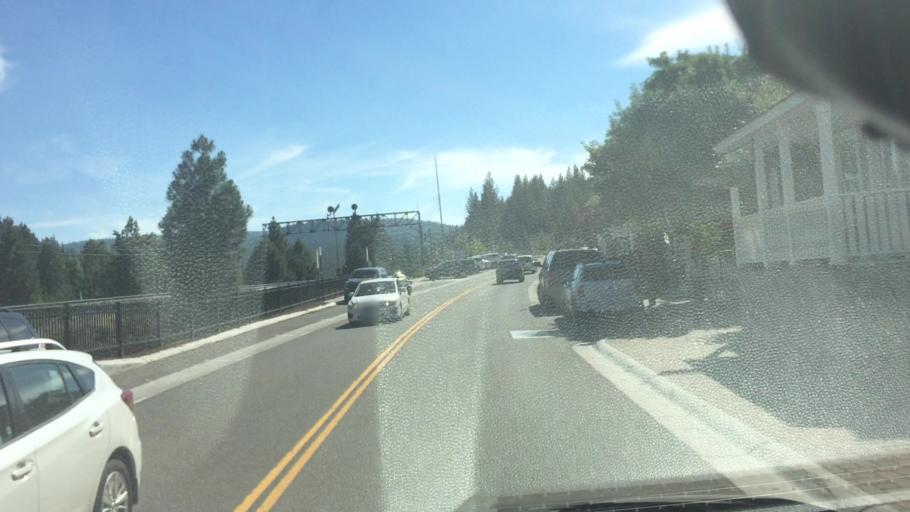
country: US
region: California
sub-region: Nevada County
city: Truckee
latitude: 39.3258
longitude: -120.1901
